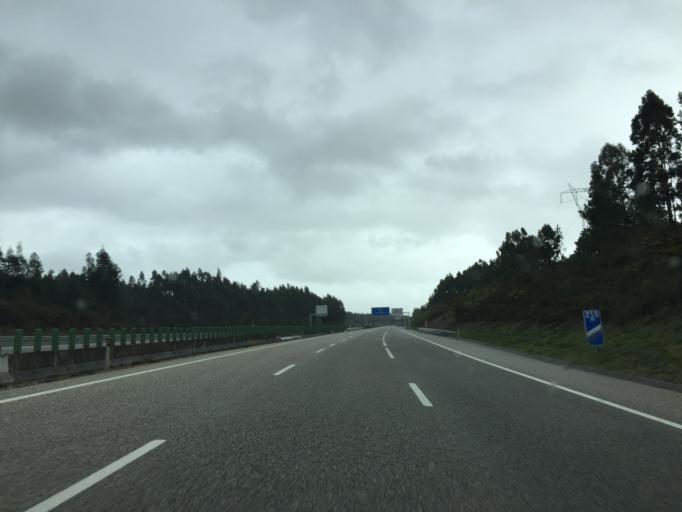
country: PT
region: Leiria
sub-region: Pombal
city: Lourical
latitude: 39.9508
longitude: -8.7715
